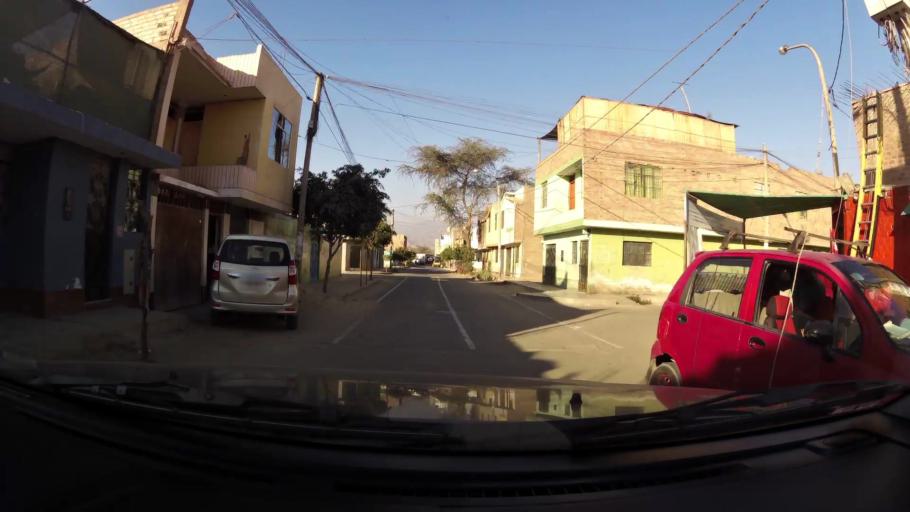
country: PE
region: Ica
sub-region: Provincia de Ica
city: Ica
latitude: -14.0696
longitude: -75.7170
